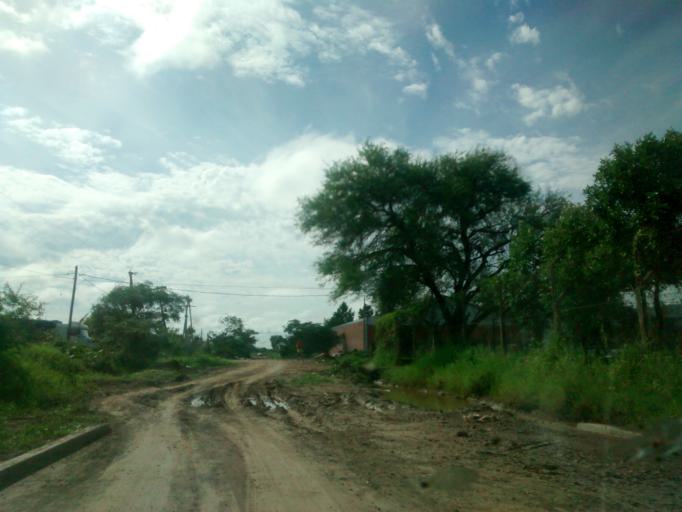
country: AR
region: Chaco
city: Fontana
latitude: -27.4059
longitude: -58.9802
